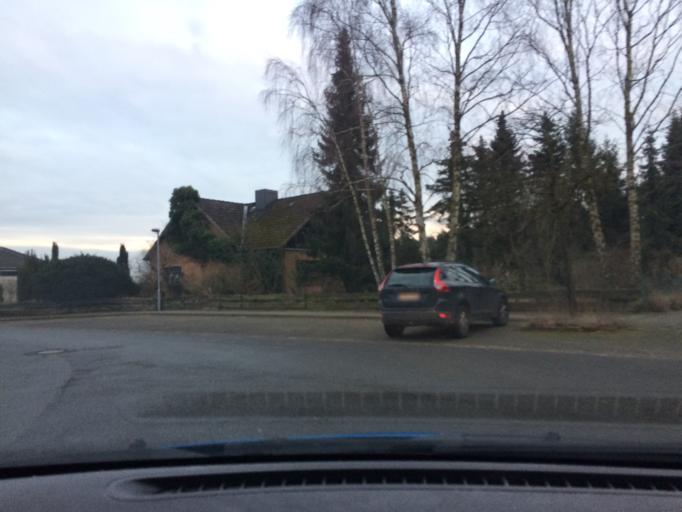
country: DE
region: Lower Saxony
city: Wendisch Evern
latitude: 53.2279
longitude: 10.4451
